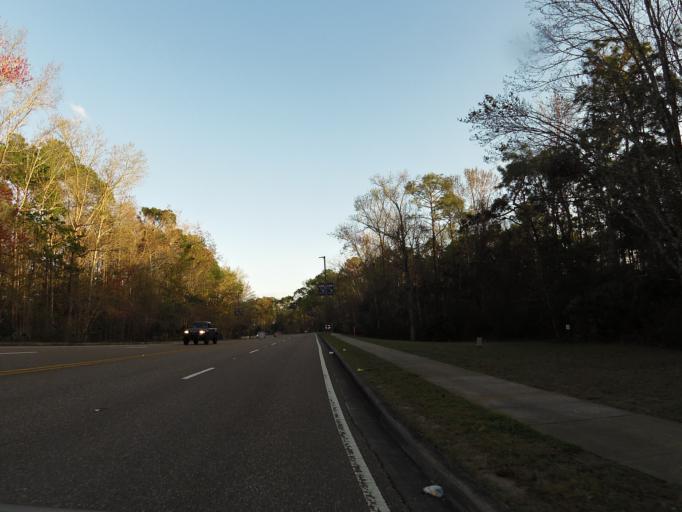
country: US
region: Florida
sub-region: Duval County
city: Jacksonville Beach
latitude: 30.2687
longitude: -81.5156
